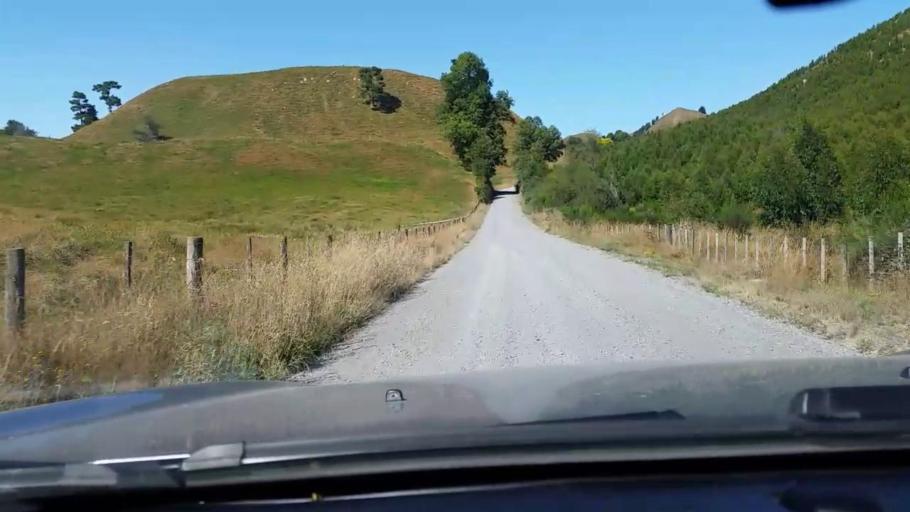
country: NZ
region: Bay of Plenty
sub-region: Rotorua District
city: Rotorua
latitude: -38.3590
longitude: 176.2123
